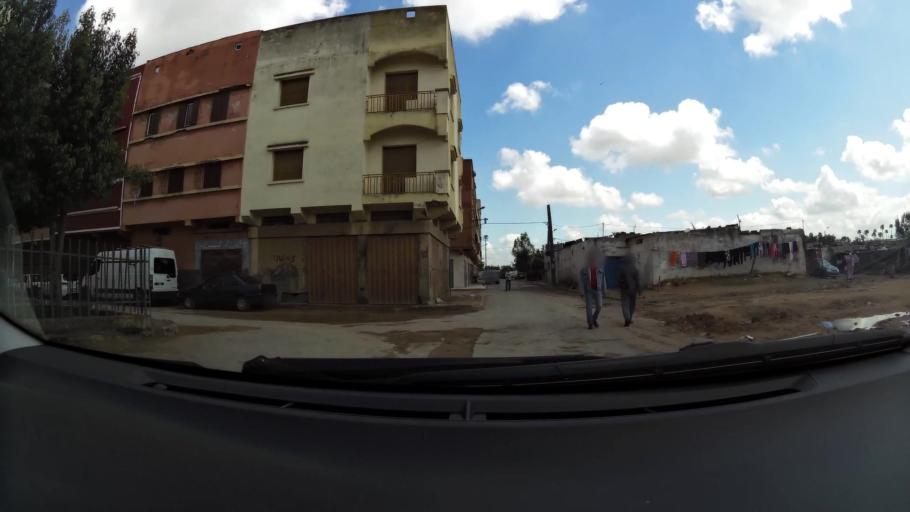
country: MA
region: Grand Casablanca
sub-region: Casablanca
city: Casablanca
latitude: 33.5427
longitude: -7.5622
